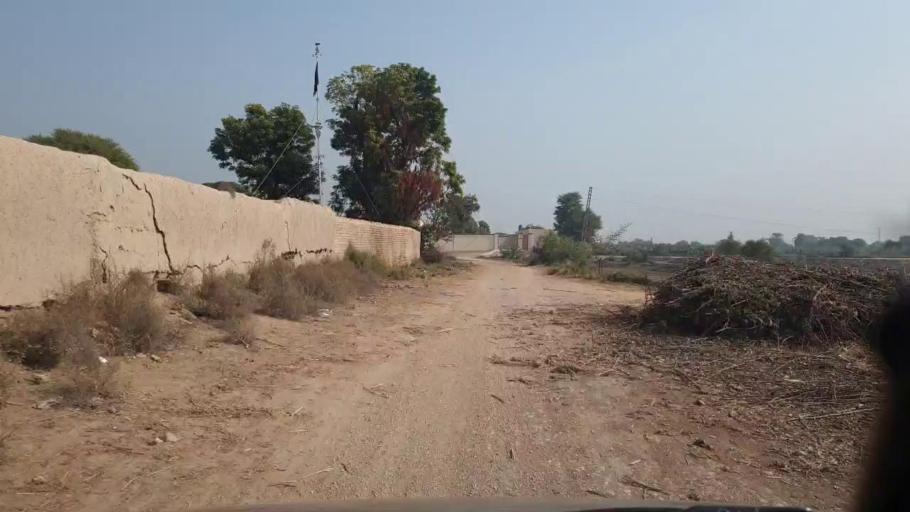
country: PK
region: Sindh
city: Shahdadpur
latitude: 26.0370
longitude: 68.5070
